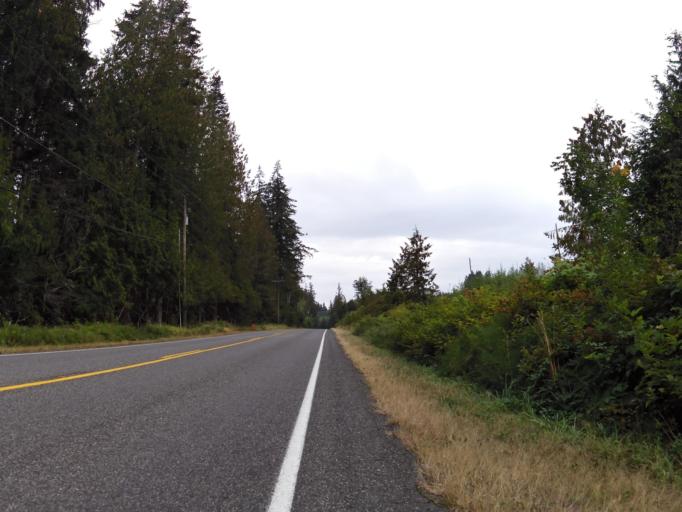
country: US
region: Washington
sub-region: Jefferson County
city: Port Ludlow
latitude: 47.9762
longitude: -122.7096
